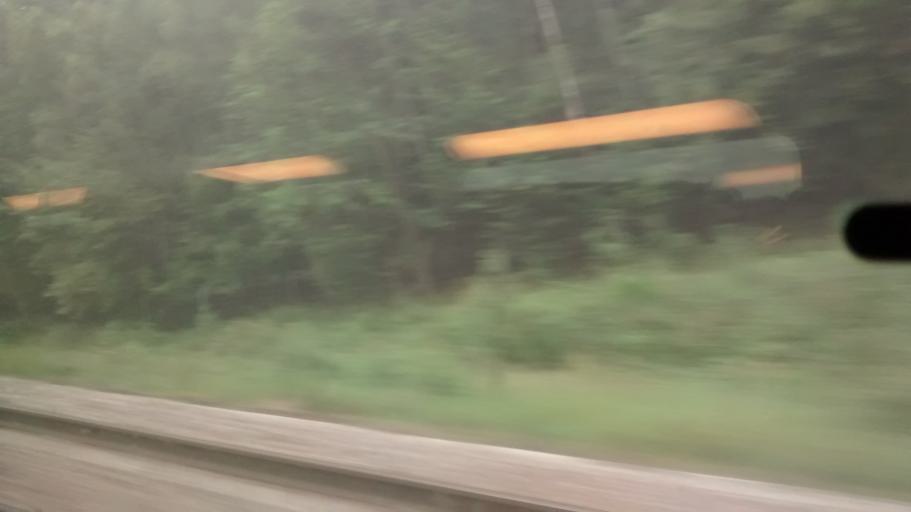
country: FR
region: Bourgogne
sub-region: Departement de l'Yonne
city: Migennes
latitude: 48.0821
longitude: 3.5299
